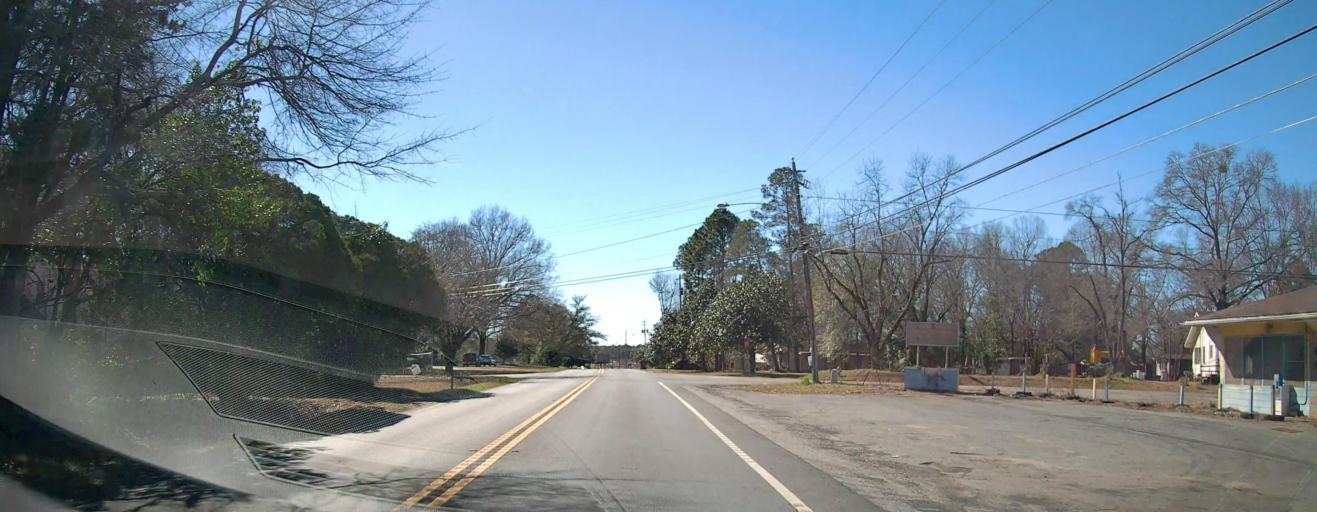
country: US
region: Georgia
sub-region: Peach County
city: Fort Valley
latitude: 32.5480
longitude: -83.8948
